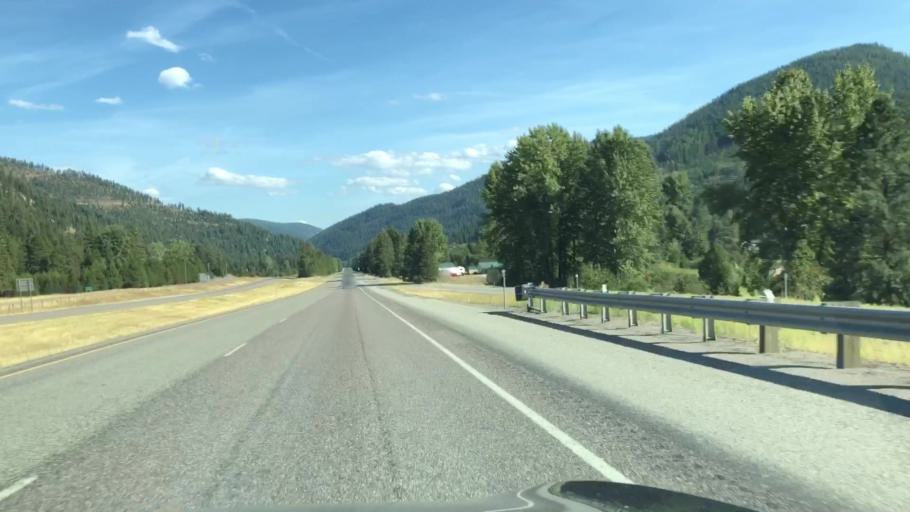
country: US
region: Montana
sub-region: Sanders County
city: Thompson Falls
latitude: 47.3749
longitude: -115.3483
